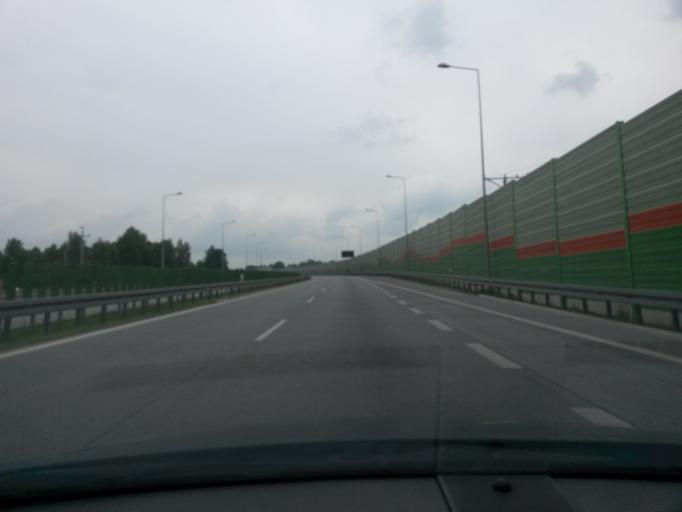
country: PL
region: Lodz Voivodeship
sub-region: Powiat rawski
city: Rawa Mazowiecka
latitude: 51.7471
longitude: 20.2409
